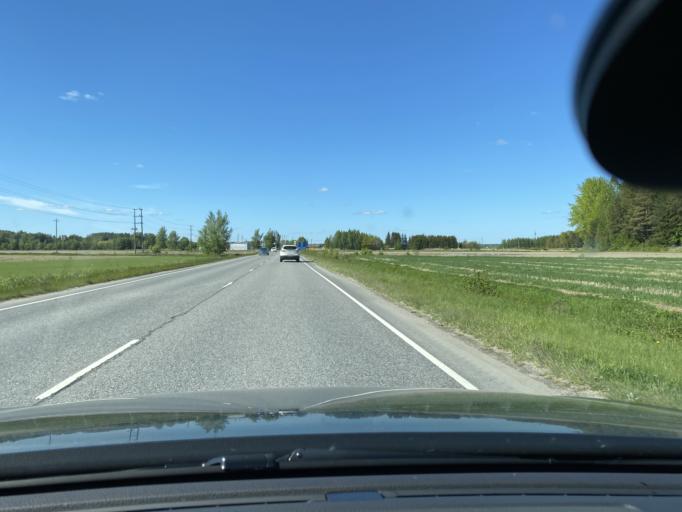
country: FI
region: Varsinais-Suomi
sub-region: Turku
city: Paimio
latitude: 60.4157
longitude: 22.6640
